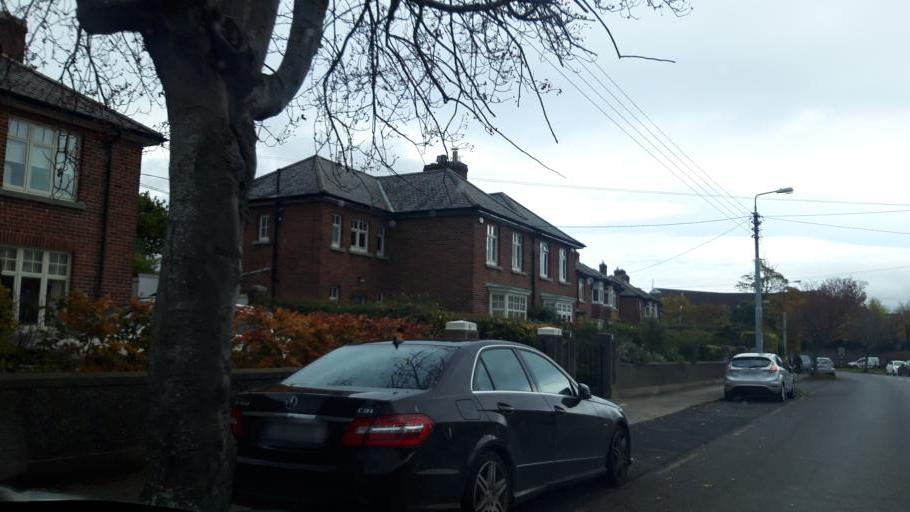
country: IE
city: Milltown
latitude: 53.3126
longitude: -6.2407
